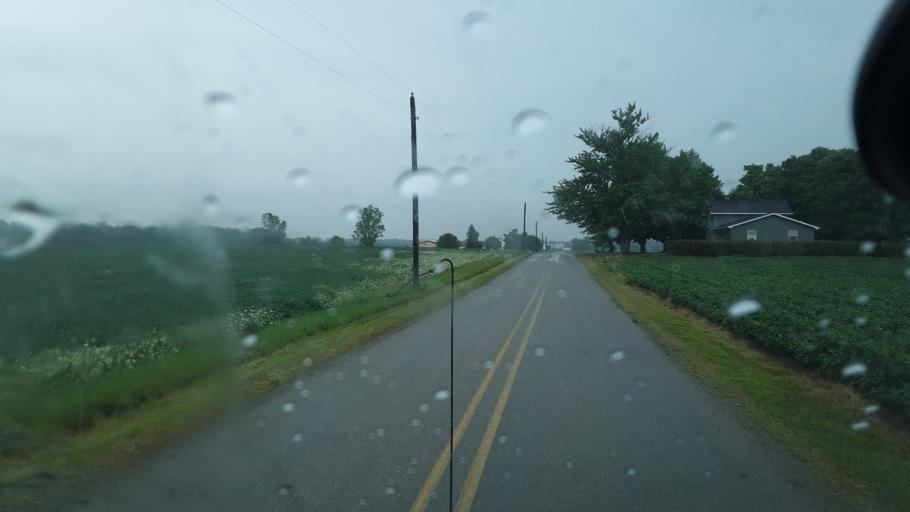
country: US
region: Indiana
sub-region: DeKalb County
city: Butler
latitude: 41.4519
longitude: -84.8137
